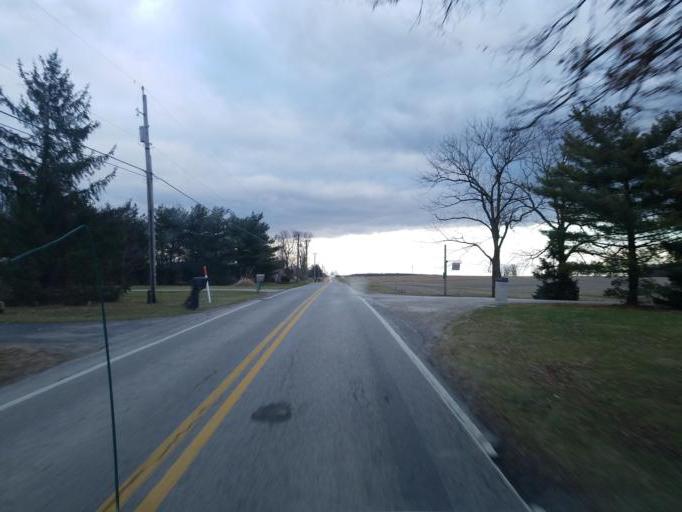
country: US
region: Ohio
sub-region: Delaware County
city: Delaware
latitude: 40.3356
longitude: -83.1191
